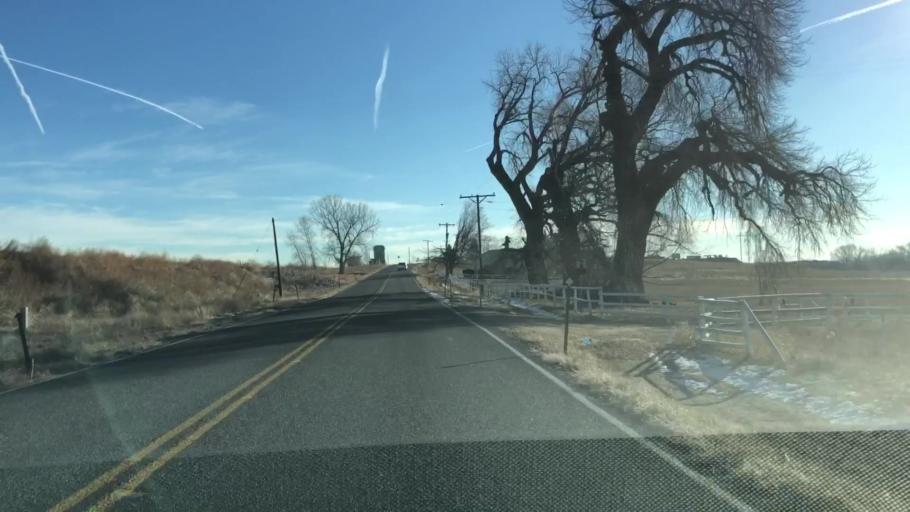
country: US
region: Colorado
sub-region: Larimer County
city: Loveland
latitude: 40.3997
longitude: -104.9992
